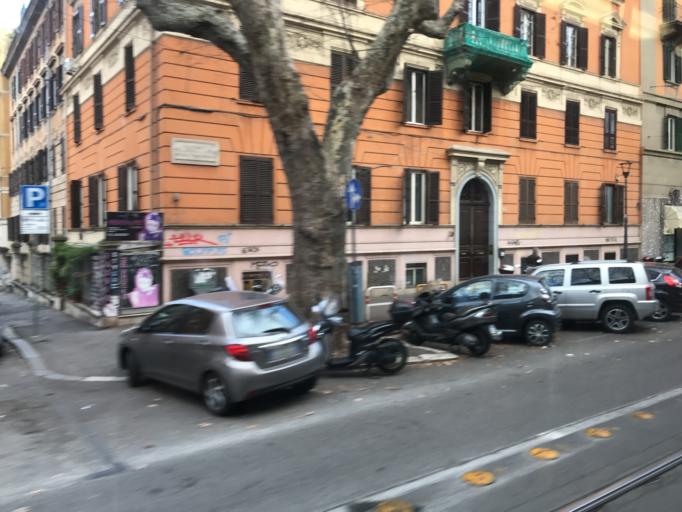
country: IT
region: Latium
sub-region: Citta metropolitana di Roma Capitale
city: Rome
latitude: 41.9154
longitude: 12.5036
